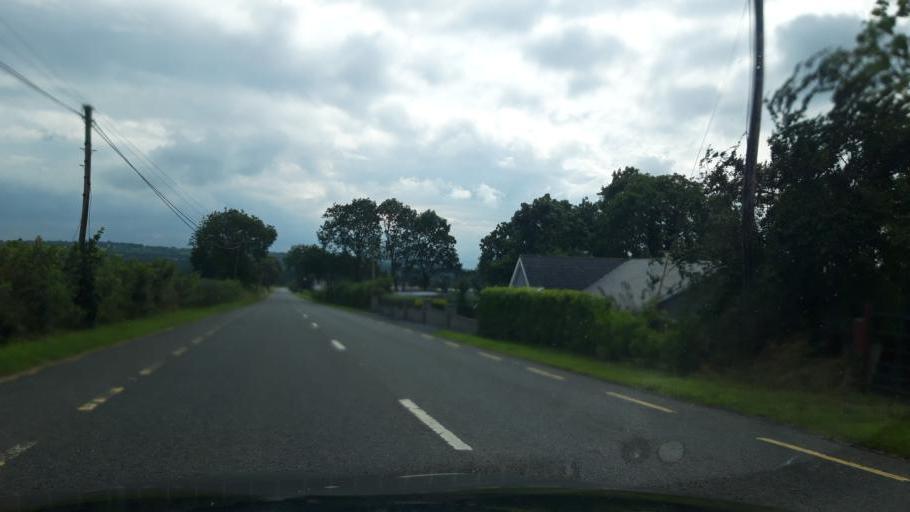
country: IE
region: Leinster
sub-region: Kilkenny
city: Castlecomer
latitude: 52.8537
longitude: -7.1193
